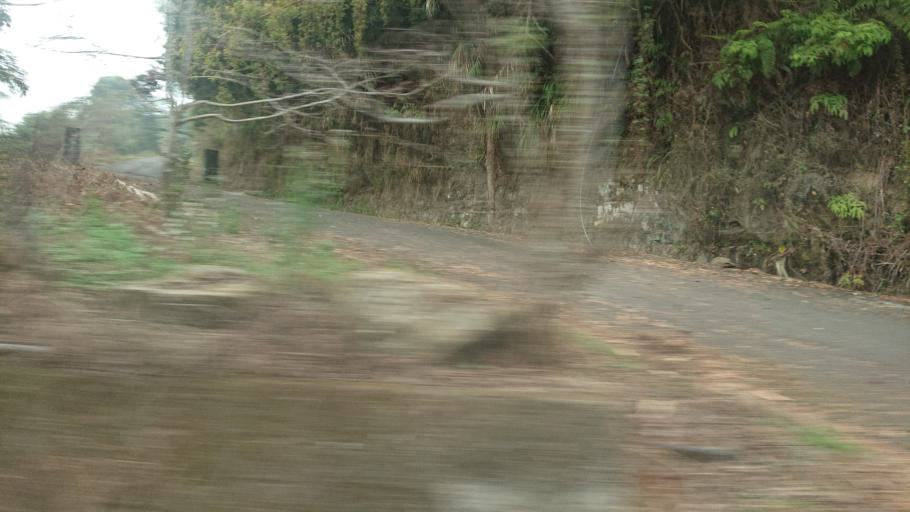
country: TW
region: Taiwan
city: Lugu
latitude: 23.6109
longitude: 120.7131
